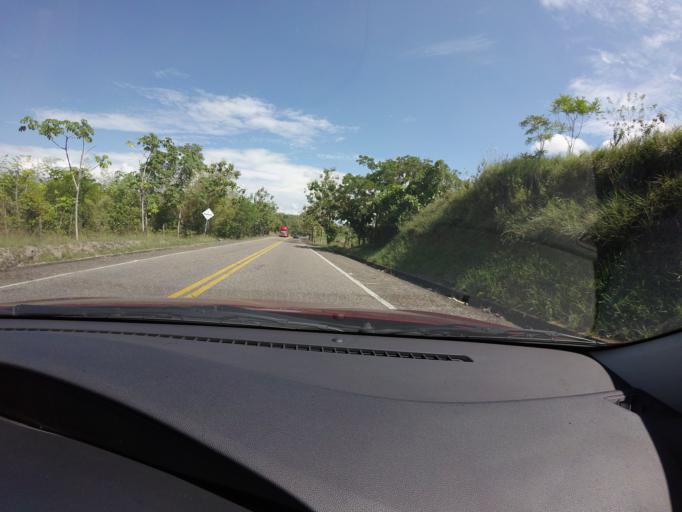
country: CO
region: Antioquia
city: Puerto Triunfo
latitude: 5.9001
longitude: -74.6314
